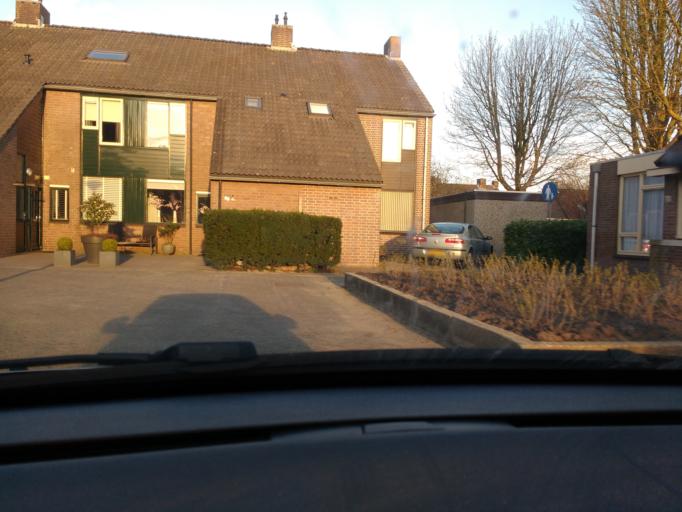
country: NL
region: Utrecht
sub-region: Gemeente Vianen
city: Vianen
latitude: 51.9843
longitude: 5.0746
